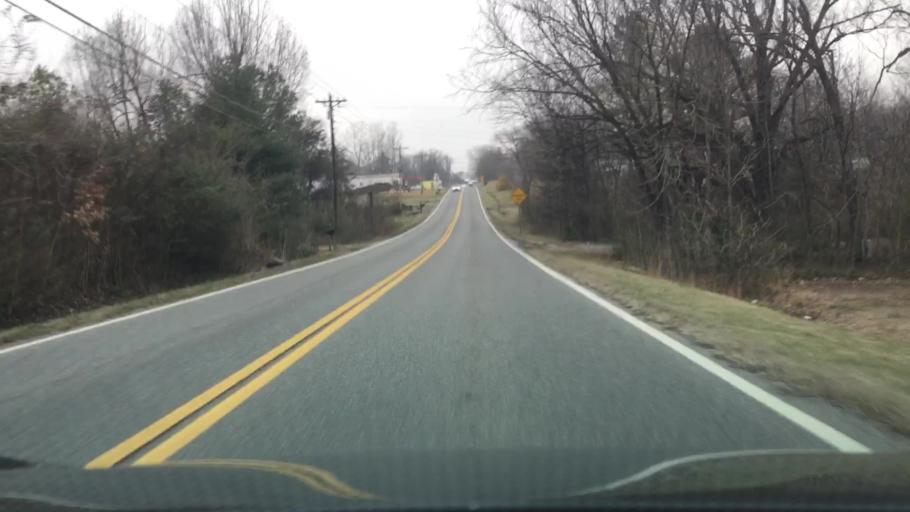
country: US
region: Kentucky
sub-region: McCracken County
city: Reidland
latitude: 36.9854
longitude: -88.4962
